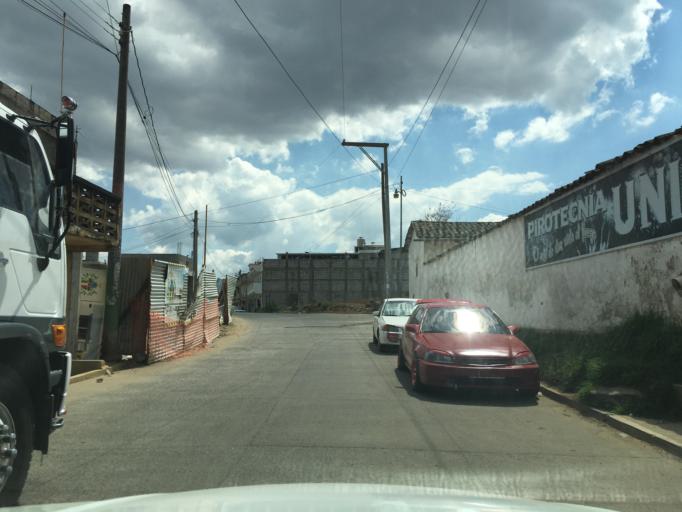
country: GT
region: Totonicapan
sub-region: Municipio de San Andres Xecul
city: San Andres Xecul
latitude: 14.9014
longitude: -91.4815
